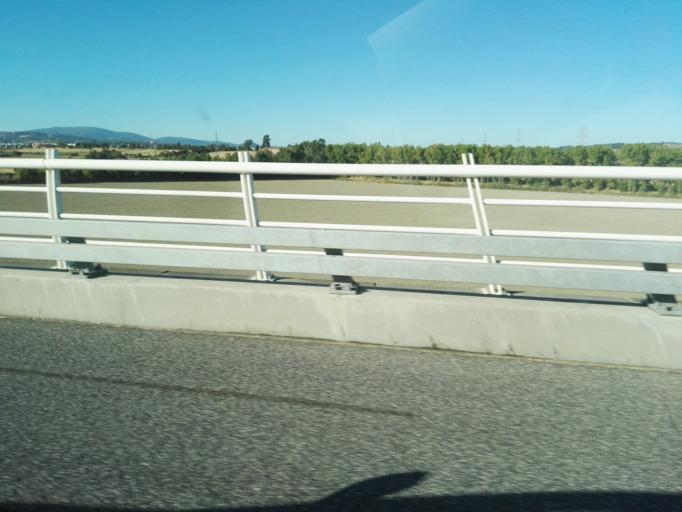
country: PT
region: Lisbon
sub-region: Alenquer
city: Carregado
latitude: 39.0168
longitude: -8.9515
